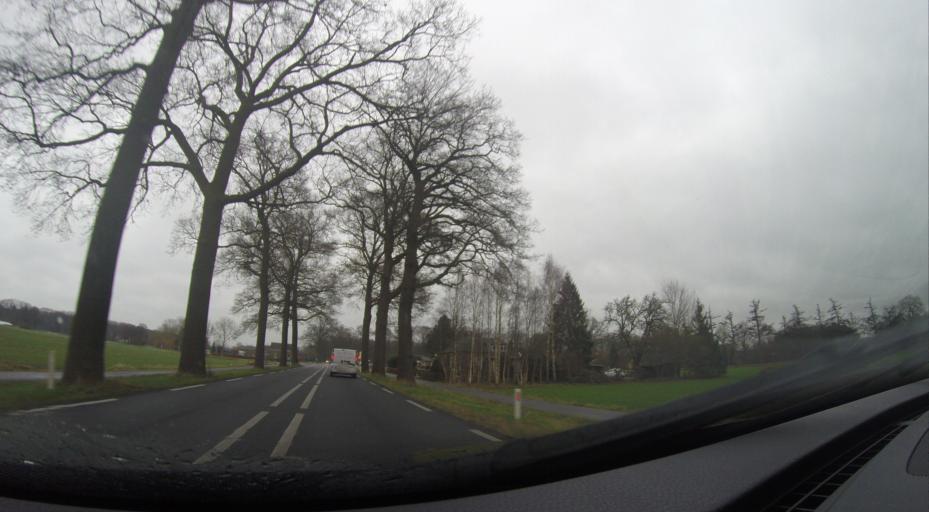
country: NL
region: Gelderland
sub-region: Gemeente Zutphen
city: Leesten
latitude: 52.1276
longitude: 6.2694
